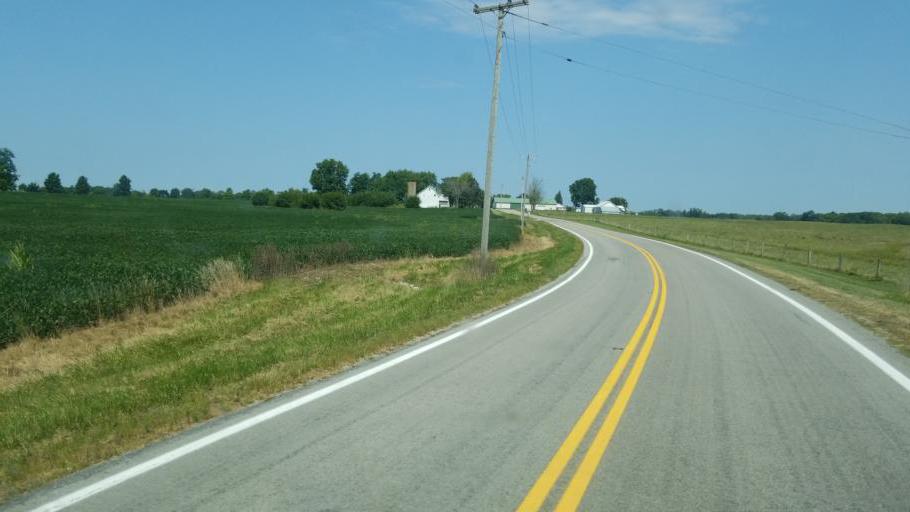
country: US
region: Ohio
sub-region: Marion County
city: Marion
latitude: 40.7222
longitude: -83.1222
